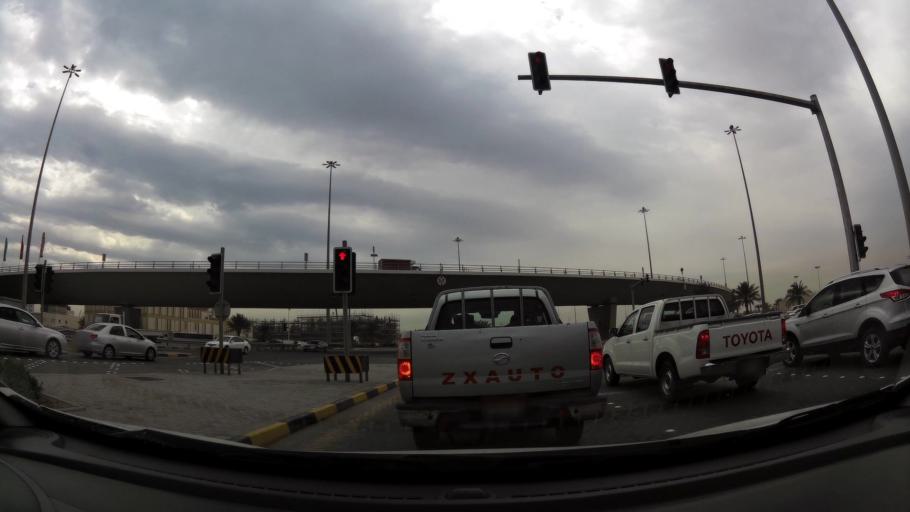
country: BH
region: Manama
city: Manama
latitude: 26.1991
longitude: 50.5907
